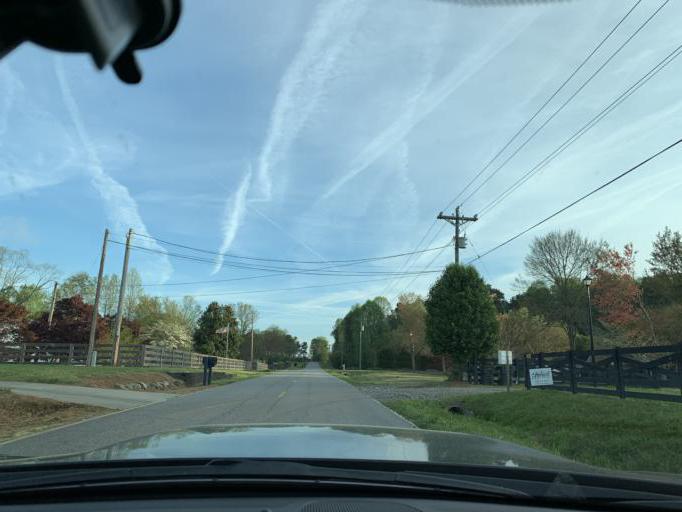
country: US
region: Georgia
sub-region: Forsyth County
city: Cumming
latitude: 34.2545
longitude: -84.1570
